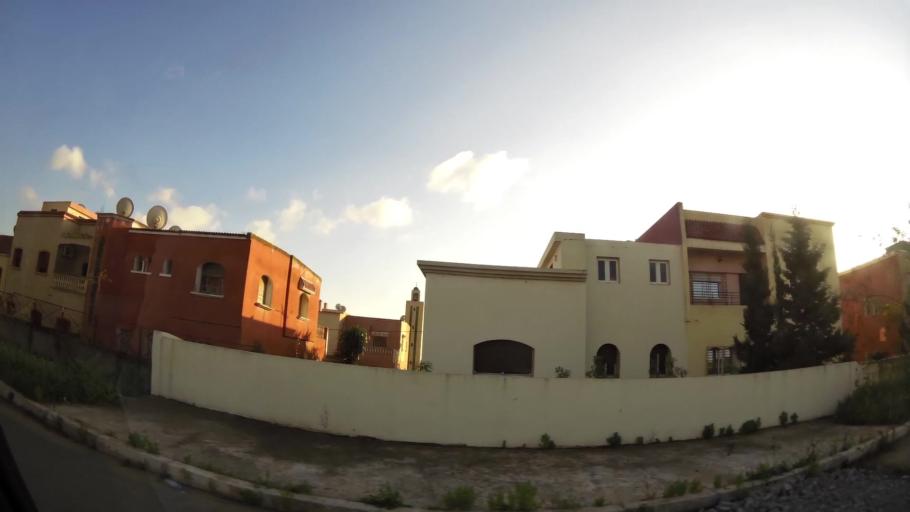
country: MA
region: Chaouia-Ouardigha
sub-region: Settat Province
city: Settat
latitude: 33.0117
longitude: -7.6025
